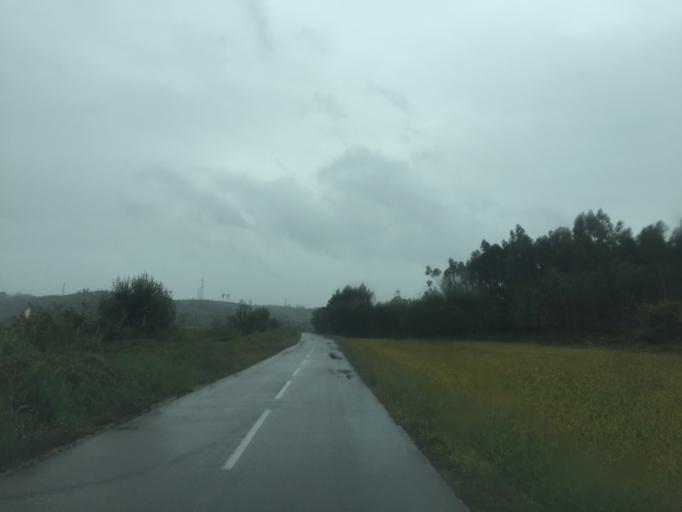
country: PT
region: Coimbra
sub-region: Figueira da Foz
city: Lavos
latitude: 40.0897
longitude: -8.8087
